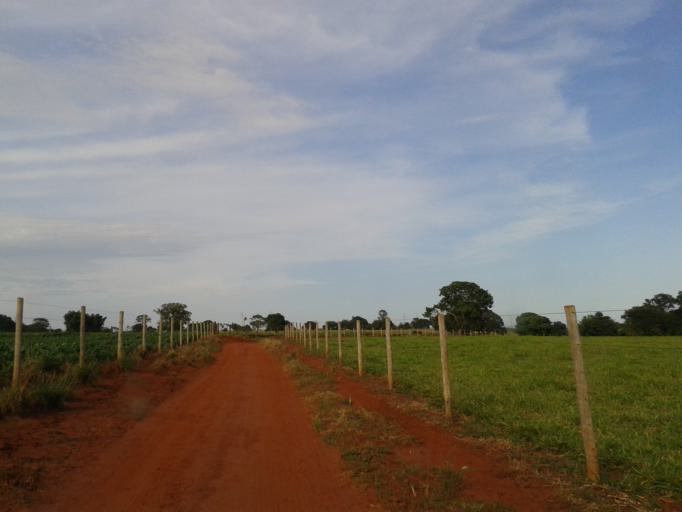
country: BR
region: Minas Gerais
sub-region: Centralina
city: Centralina
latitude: -18.7127
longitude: -49.1927
